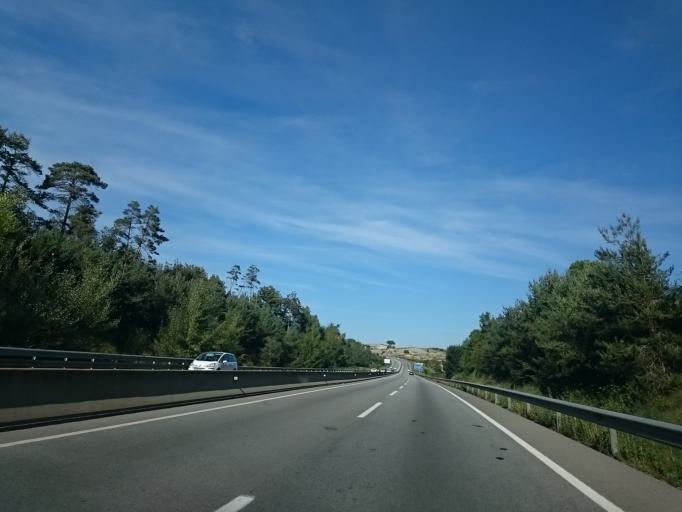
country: ES
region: Catalonia
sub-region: Provincia de Barcelona
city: Centelles
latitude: 41.8137
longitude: 2.2284
